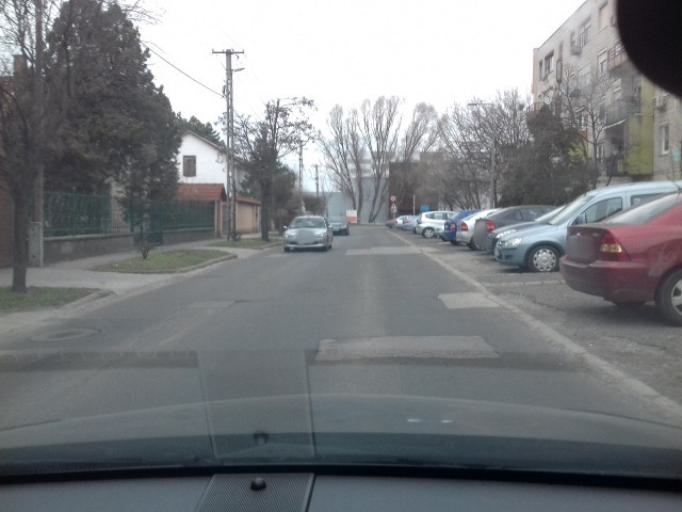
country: HU
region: Budapest
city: Budapest XVI. keruelet
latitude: 47.5263
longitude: 19.1482
